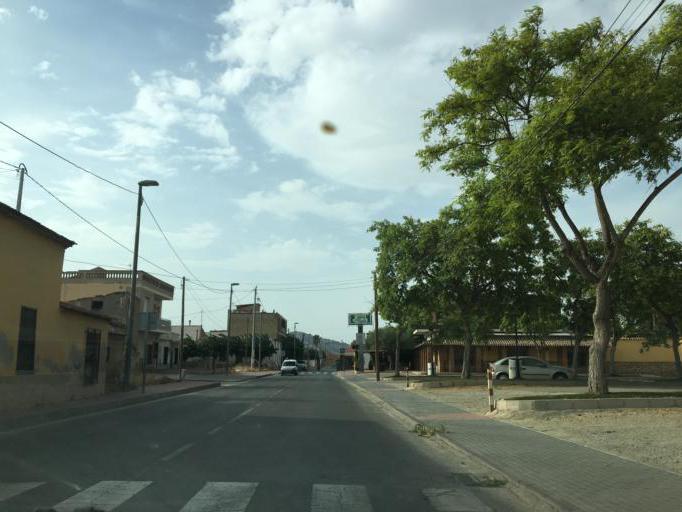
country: ES
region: Murcia
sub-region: Murcia
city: Murcia
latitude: 38.0091
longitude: -1.0803
